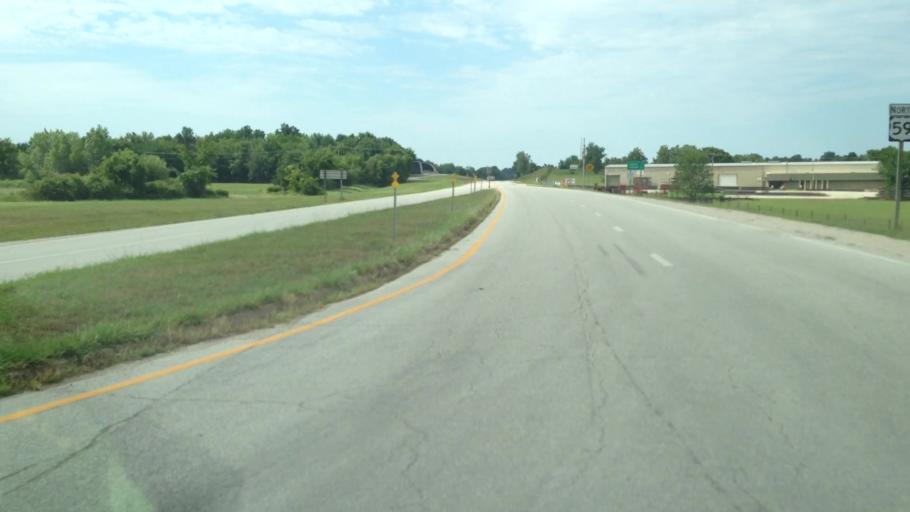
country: US
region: Kansas
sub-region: Labette County
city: Chetopa
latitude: 37.0484
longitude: -95.1004
